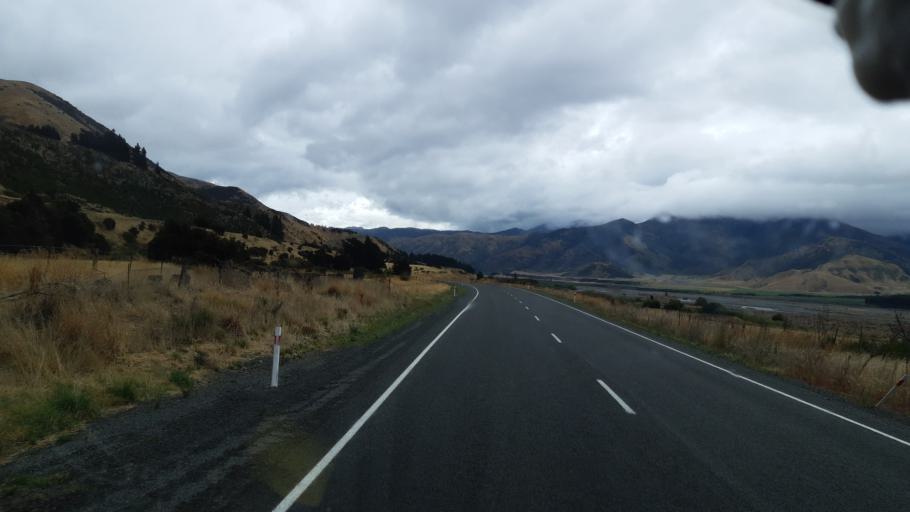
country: NZ
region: Canterbury
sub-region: Hurunui District
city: Amberley
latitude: -42.5763
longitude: 172.7282
